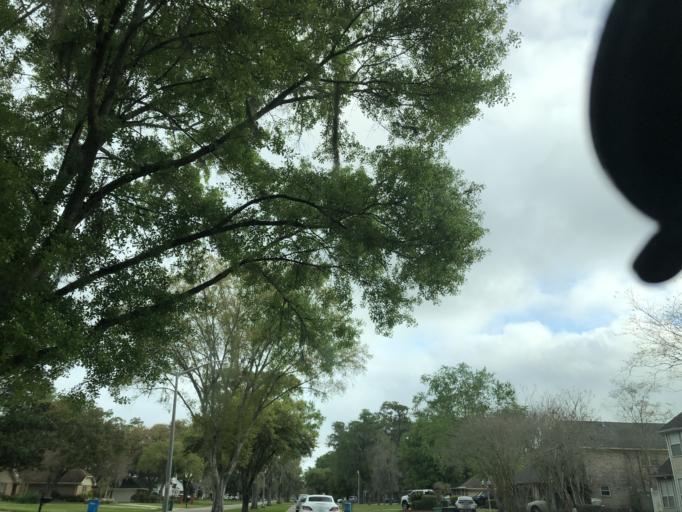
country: US
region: Louisiana
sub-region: Saint Charles Parish
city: New Sarpy
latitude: 29.9738
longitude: -90.3654
